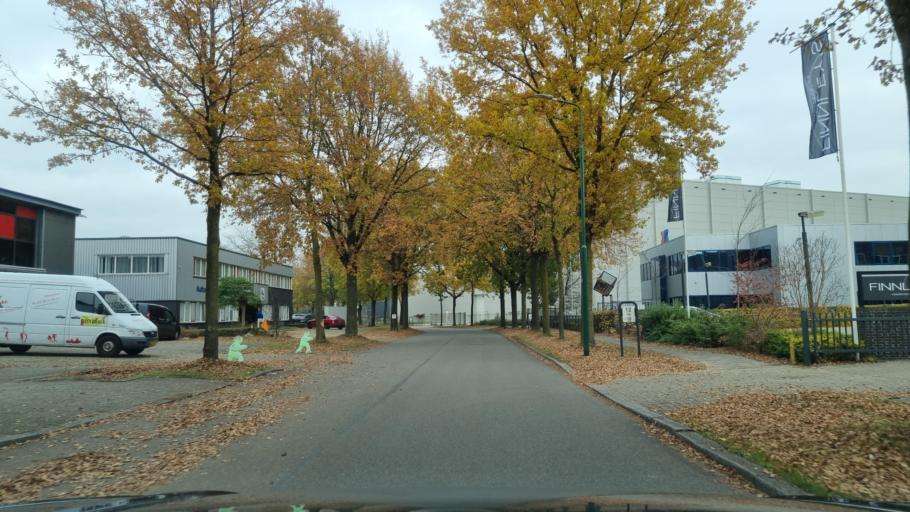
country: NL
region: Utrecht
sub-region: Gemeente Veenendaal
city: Veenendaal
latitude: 52.0387
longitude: 5.5464
